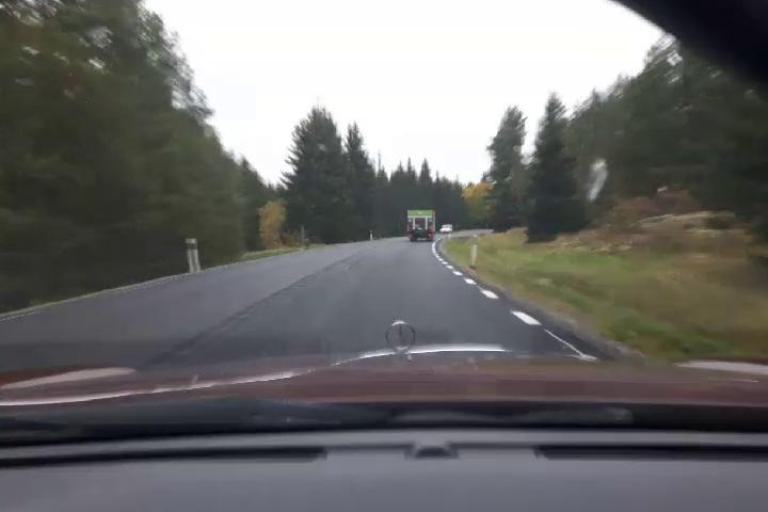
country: SE
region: Soedermanland
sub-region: Strangnas Kommun
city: Strangnas
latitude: 59.4168
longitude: 17.0197
